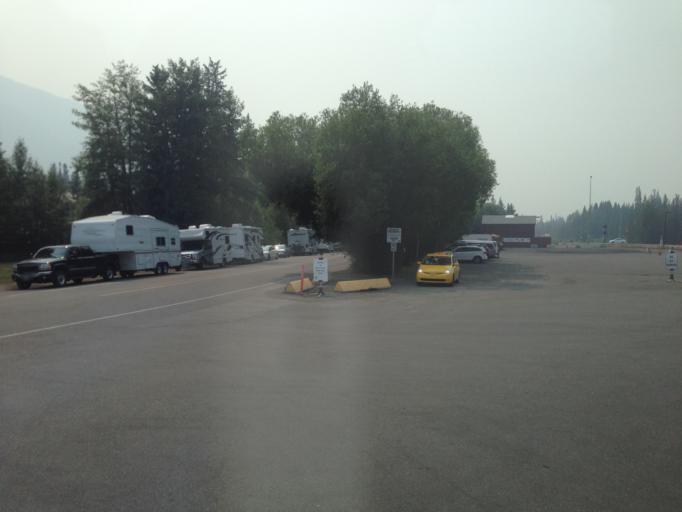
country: CA
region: Alberta
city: Banff
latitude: 51.1815
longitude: -115.5761
